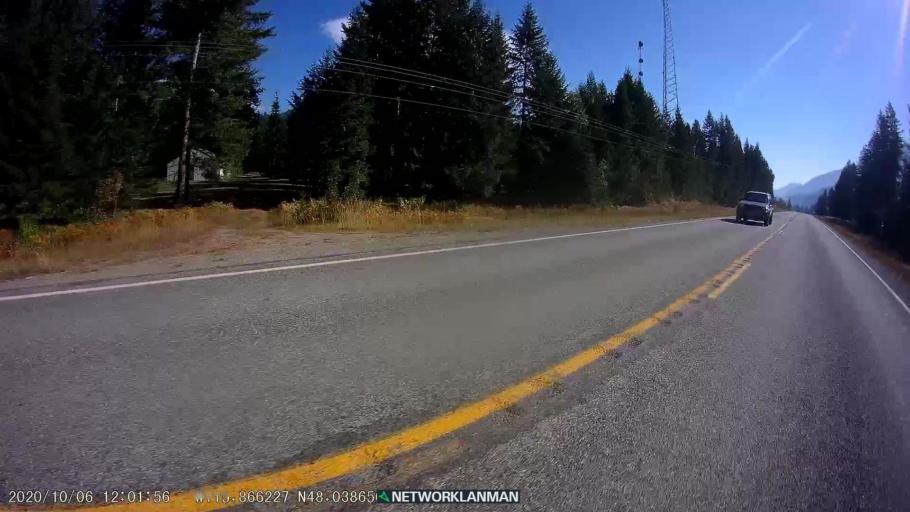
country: US
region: Montana
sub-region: Lincoln County
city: Libby
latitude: 48.0383
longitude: -115.8659
